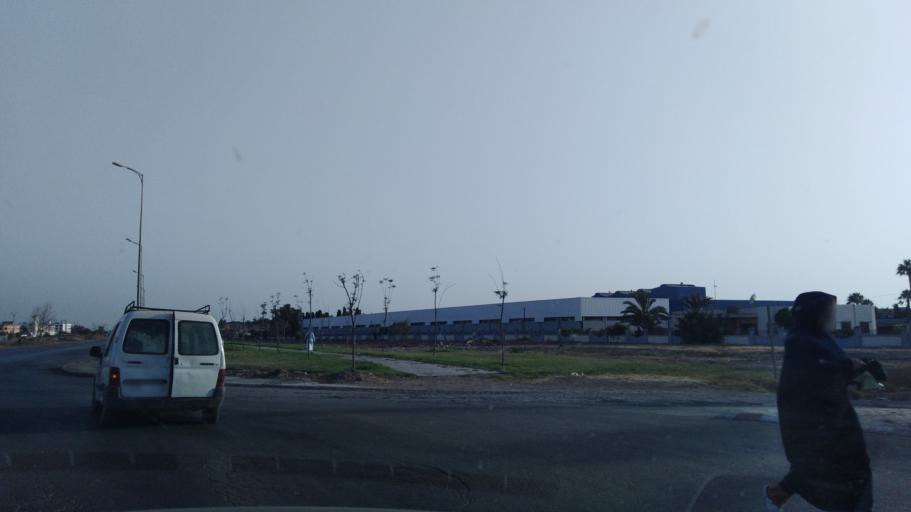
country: MA
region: Chaouia-Ouardigha
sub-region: Settat Province
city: Berrechid
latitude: 33.2442
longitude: -7.5867
